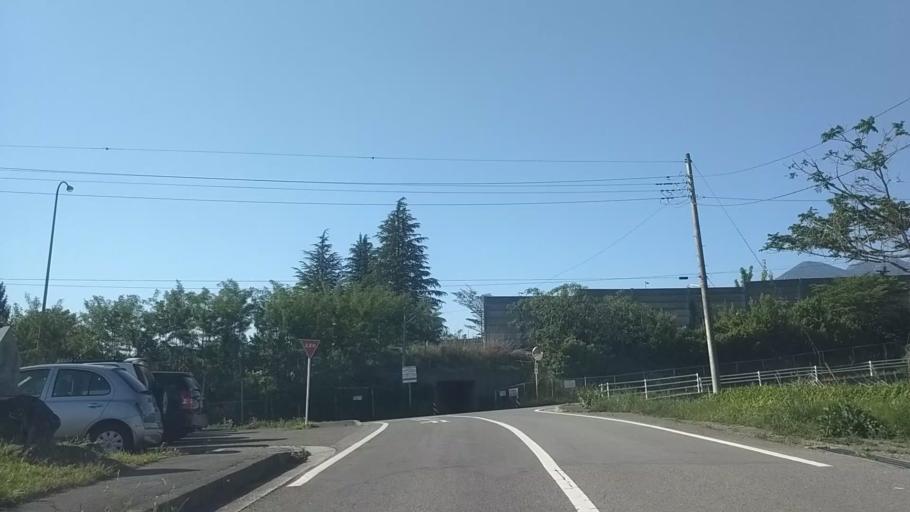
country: JP
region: Nagano
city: Chino
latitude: 35.8694
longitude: 138.3125
